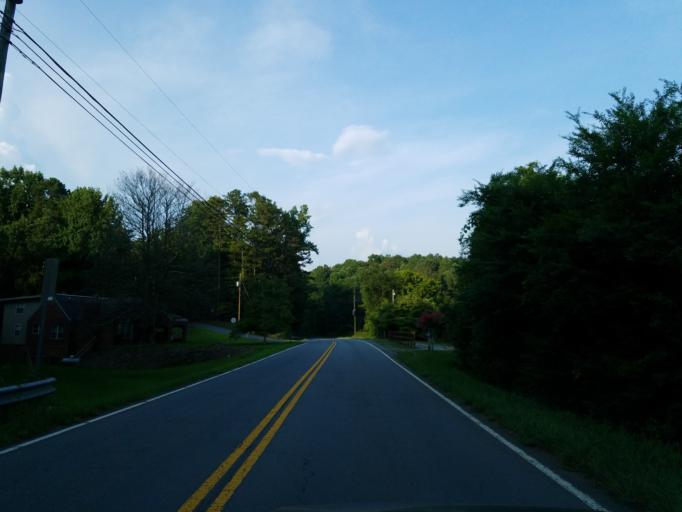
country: US
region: Georgia
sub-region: Gilmer County
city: Ellijay
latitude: 34.6150
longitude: -84.5231
